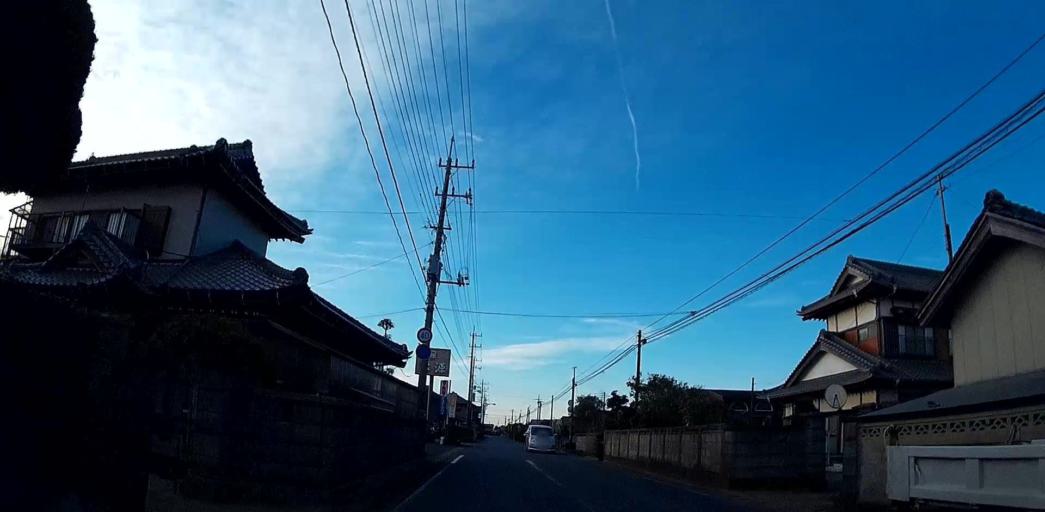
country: JP
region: Chiba
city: Omigawa
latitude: 35.8376
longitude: 140.6773
